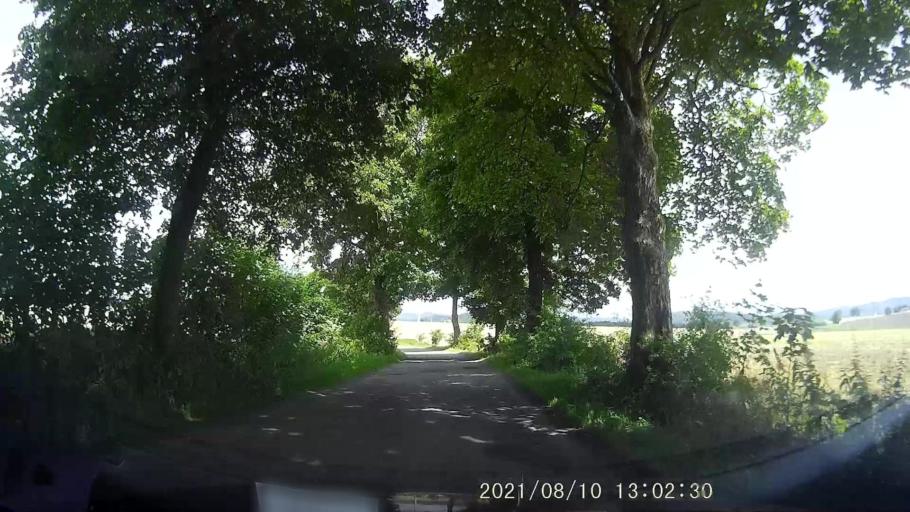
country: PL
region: Lower Silesian Voivodeship
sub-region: Powiat klodzki
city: Bozkow
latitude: 50.4650
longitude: 16.5582
